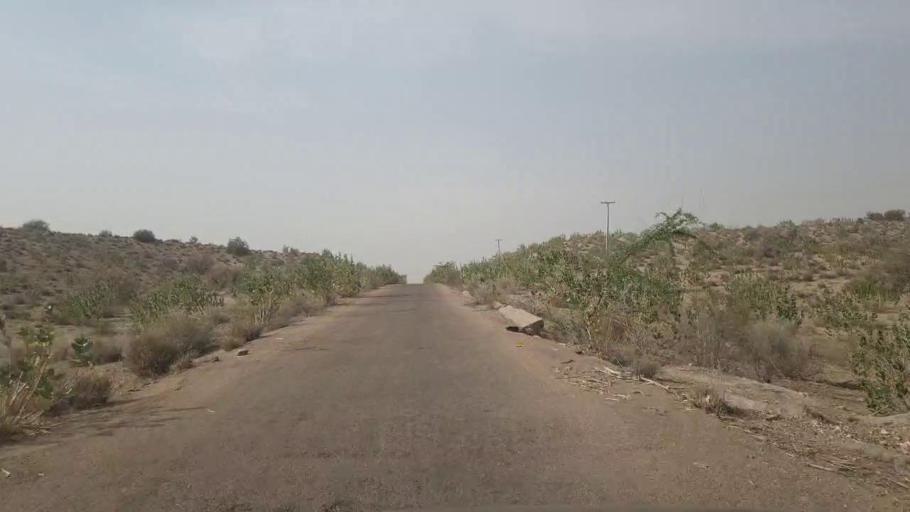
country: PK
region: Sindh
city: Chor
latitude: 25.6117
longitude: 69.9327
